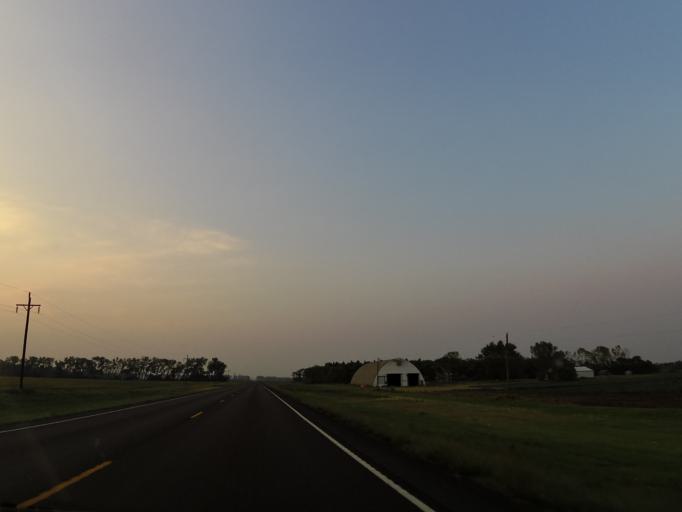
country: US
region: North Dakota
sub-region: Walsh County
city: Park River
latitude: 48.3416
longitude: -97.6223
